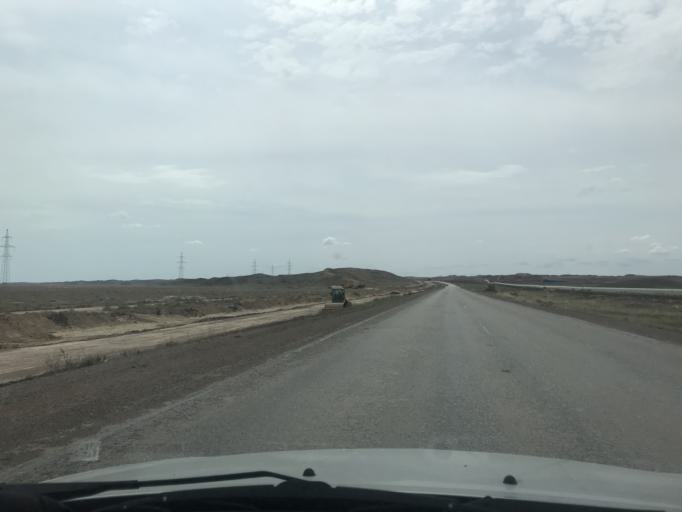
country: KZ
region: Zhambyl
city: Mynaral
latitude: 45.3776
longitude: 73.6543
